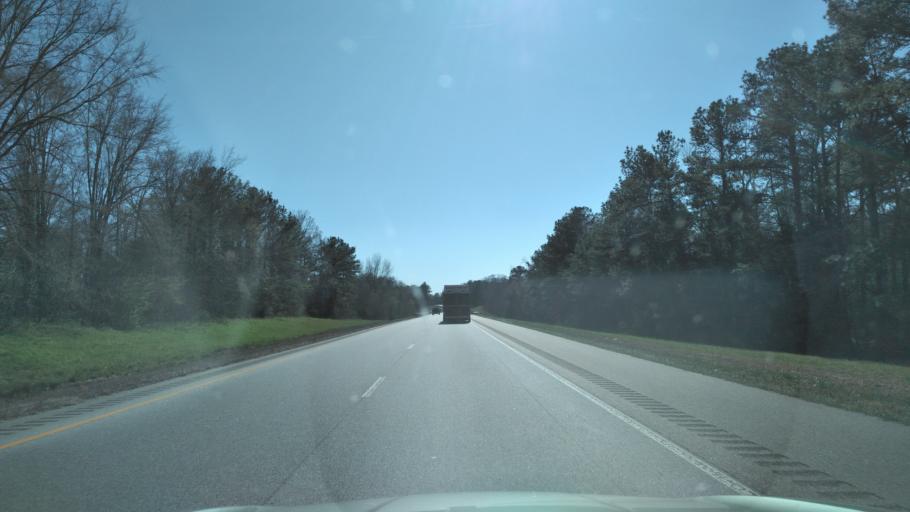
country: US
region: Alabama
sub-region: Lowndes County
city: Fort Deposit
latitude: 32.0566
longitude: -86.4945
